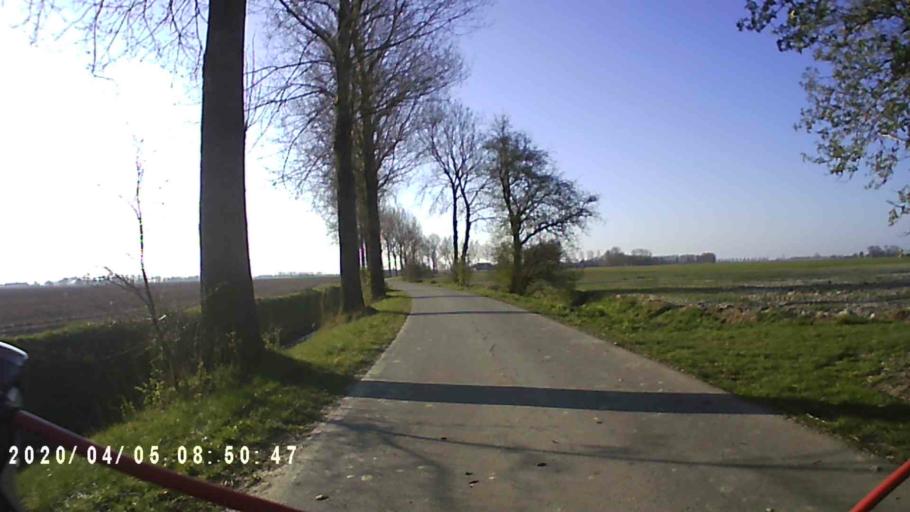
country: NL
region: Groningen
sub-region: Gemeente Winsum
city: Winsum
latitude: 53.3159
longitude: 6.4633
